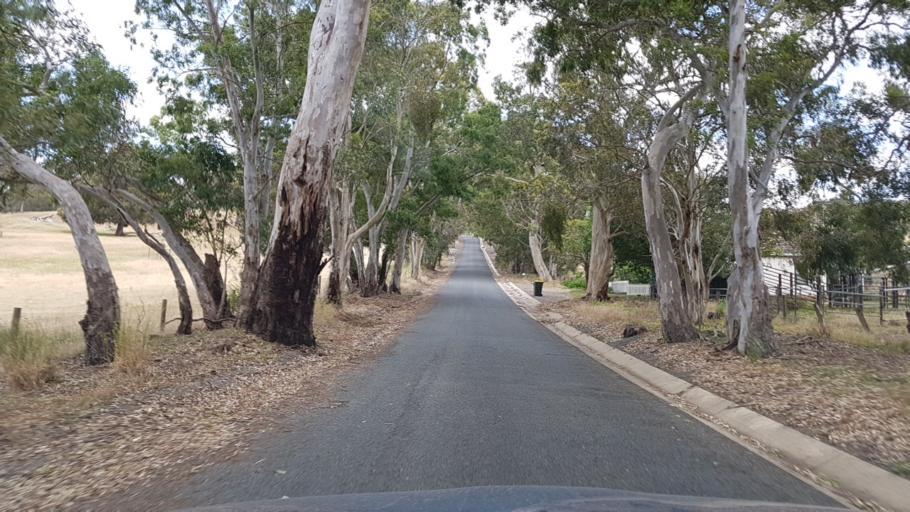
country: AU
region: South Australia
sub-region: Victor Harbor
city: Victor Harbor
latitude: -35.4653
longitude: 138.5942
